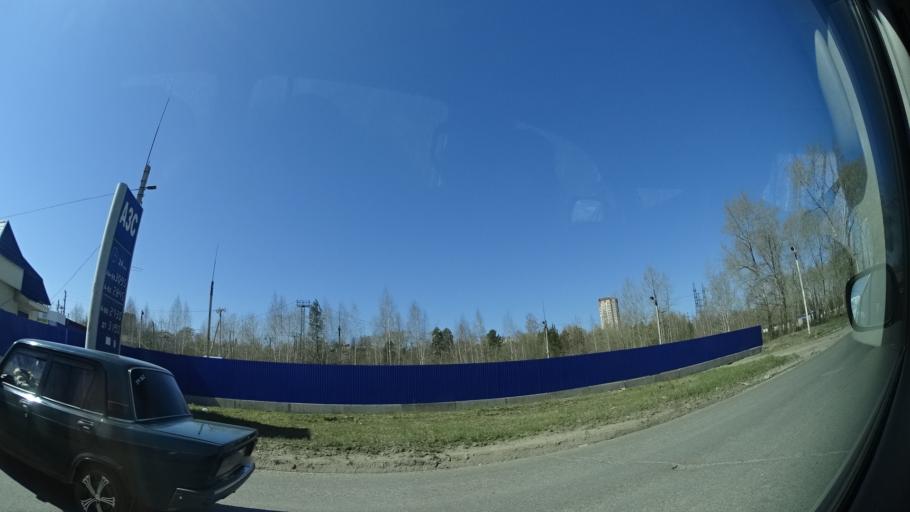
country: RU
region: Perm
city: Perm
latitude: 58.1091
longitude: 56.3220
